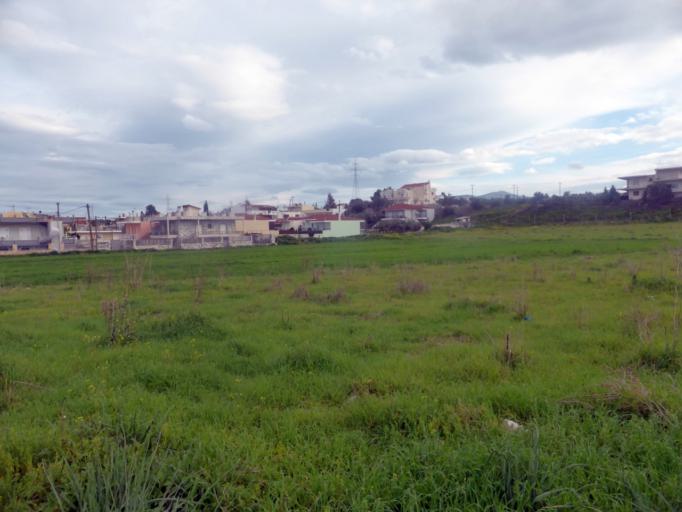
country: GR
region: Peloponnese
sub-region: Nomos Korinthias
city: Arkhaia Korinthos
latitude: 37.9294
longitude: 22.8865
